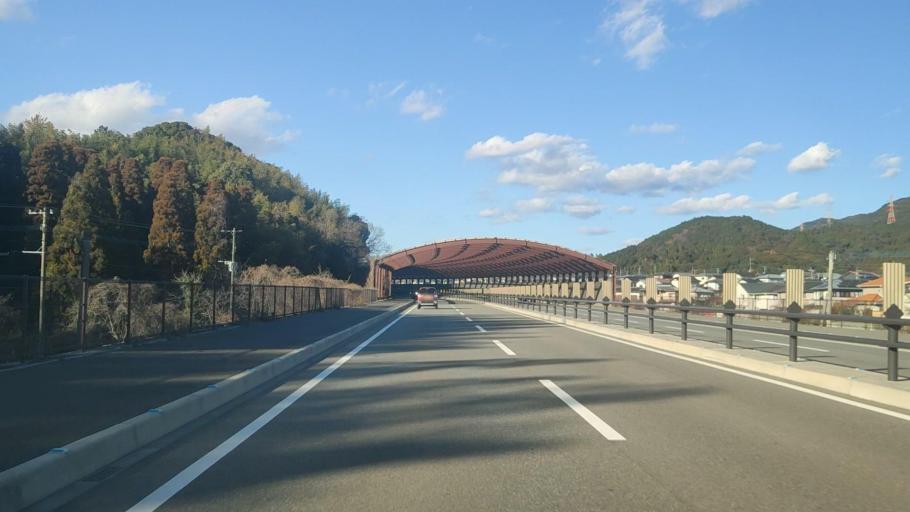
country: JP
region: Fukuoka
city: Dazaifu
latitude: 33.5091
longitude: 130.5501
